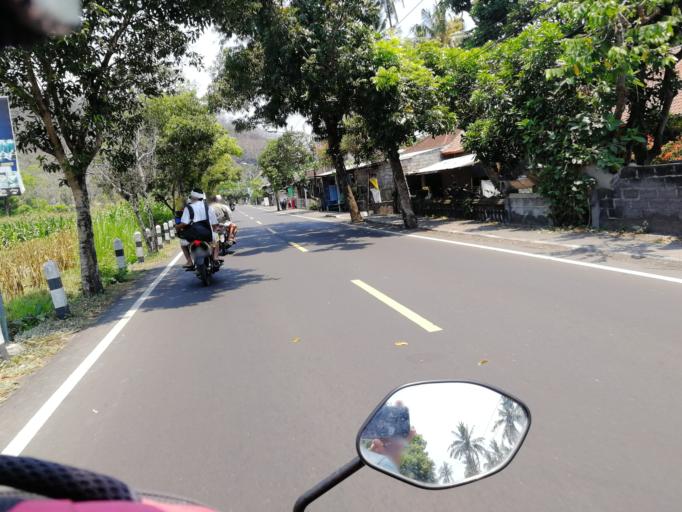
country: ID
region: Bali
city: Banjar Pegeringsingan
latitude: -8.5055
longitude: 115.5600
